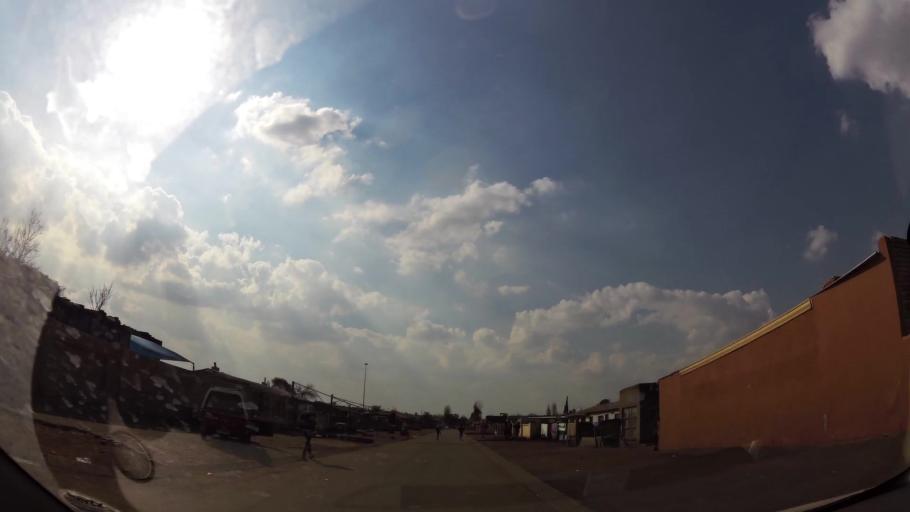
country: ZA
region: Gauteng
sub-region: Ekurhuleni Metropolitan Municipality
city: Germiston
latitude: -26.3060
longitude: 28.1509
